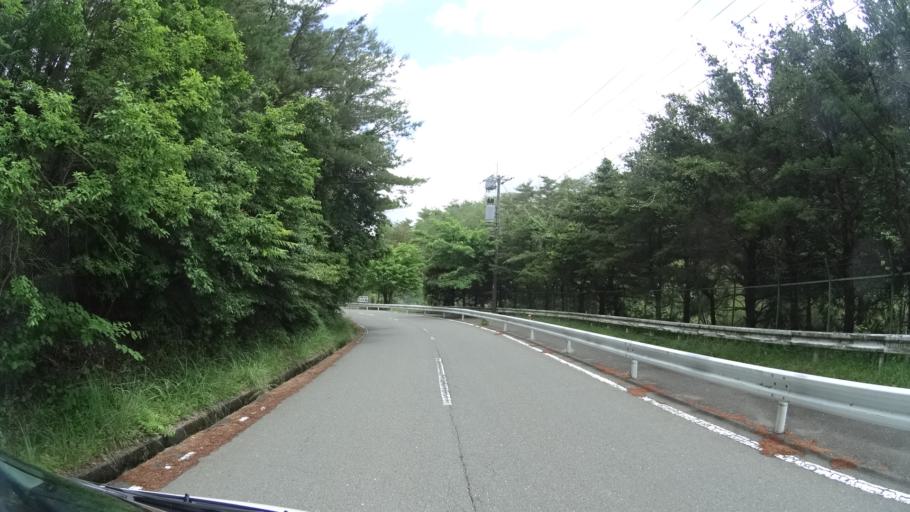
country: JP
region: Hyogo
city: Sasayama
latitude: 35.0301
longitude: 135.3916
